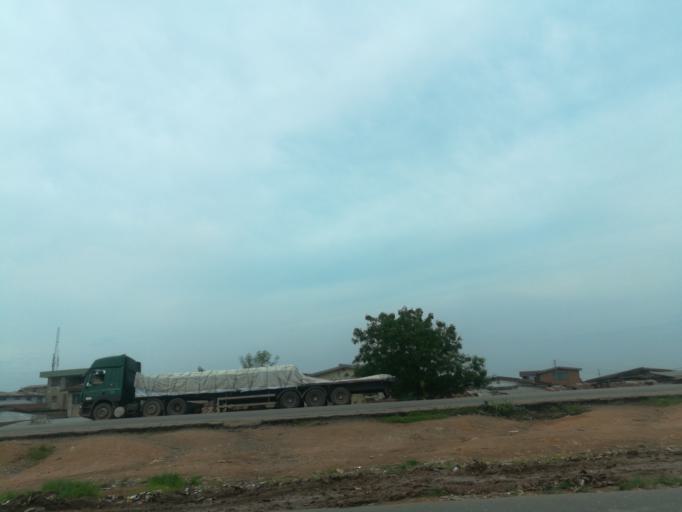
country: NG
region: Oyo
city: Ibadan
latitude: 7.3619
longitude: 3.9259
